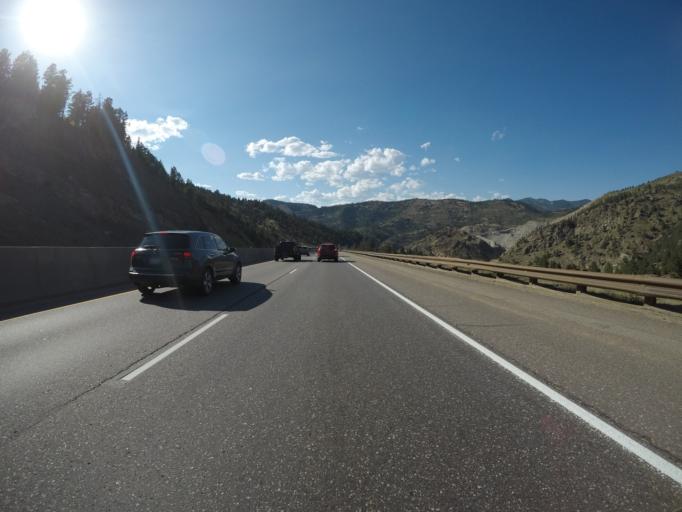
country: US
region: Colorado
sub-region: Clear Creek County
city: Idaho Springs
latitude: 39.7360
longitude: -105.4296
